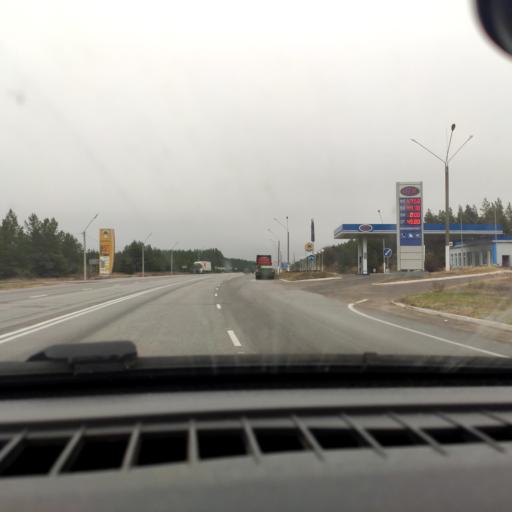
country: RU
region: Voronezj
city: Uryv-Pokrovka
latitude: 51.0459
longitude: 38.9818
